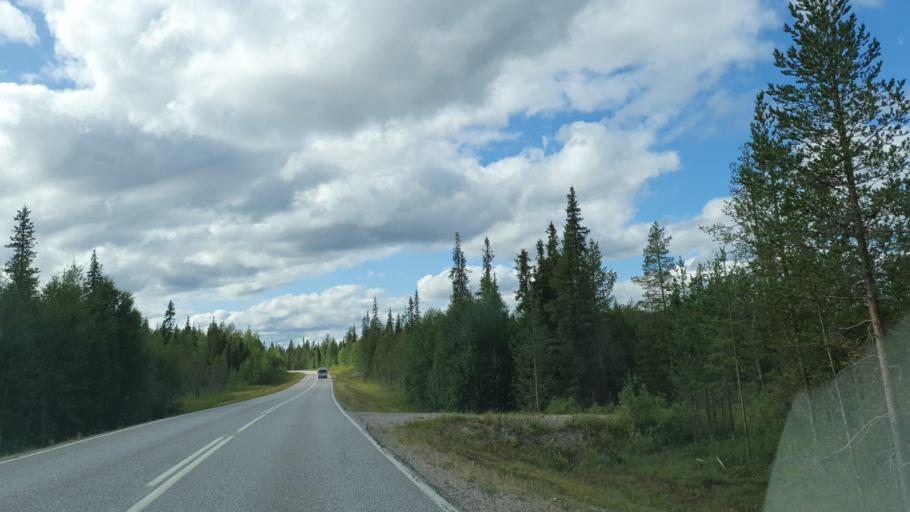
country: FI
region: Lapland
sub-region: Tunturi-Lappi
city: Muonio
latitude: 67.8715
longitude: 24.1866
